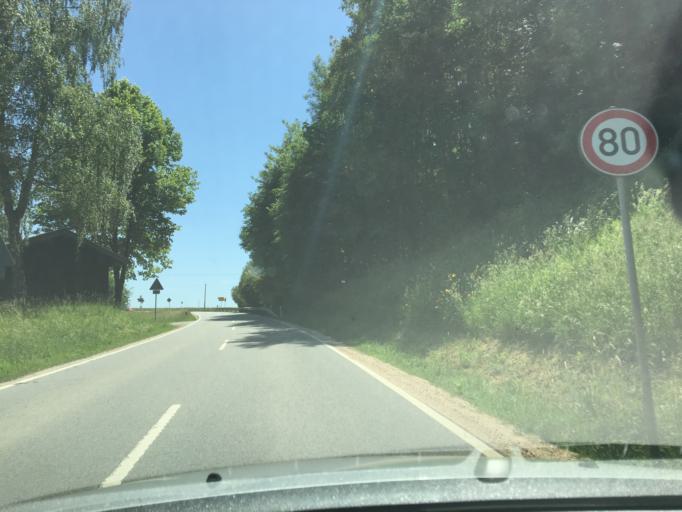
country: DE
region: Bavaria
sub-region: Upper Bavaria
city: Halsbach
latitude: 48.1337
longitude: 12.6511
